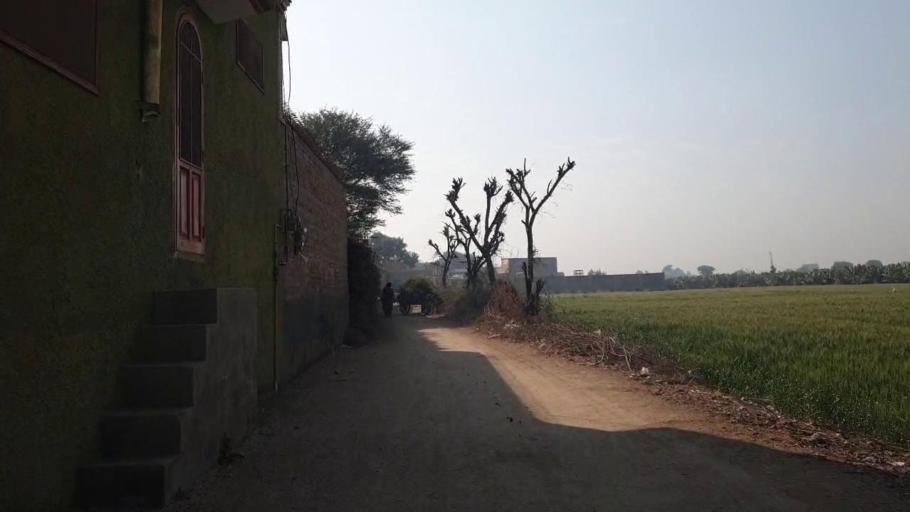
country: PK
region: Sindh
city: Chambar
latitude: 25.3758
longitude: 68.7752
